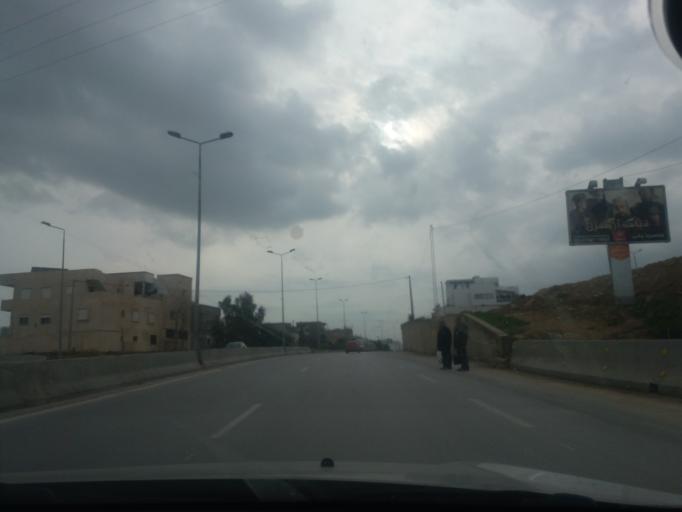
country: TN
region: Ariana
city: Ariana
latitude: 36.8657
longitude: 10.1784
